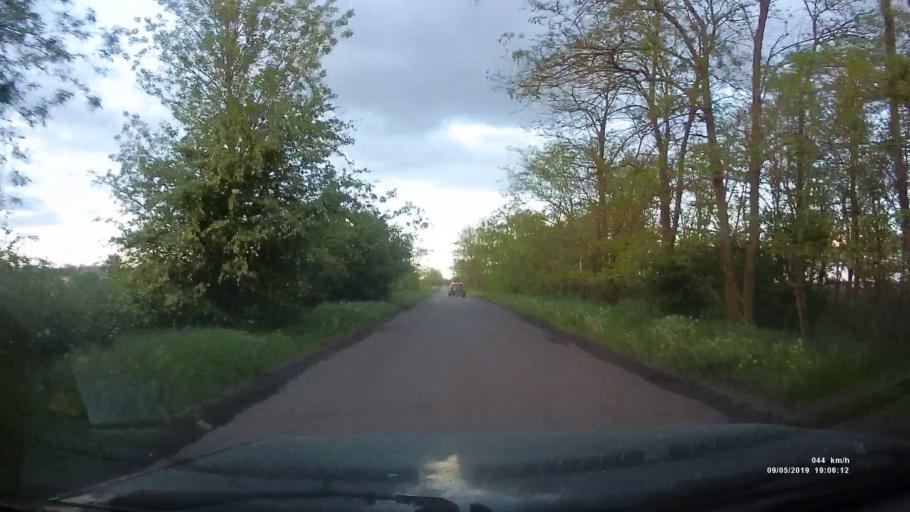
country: RU
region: Krasnodarskiy
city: Kanelovskaya
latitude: 46.7384
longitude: 39.1884
